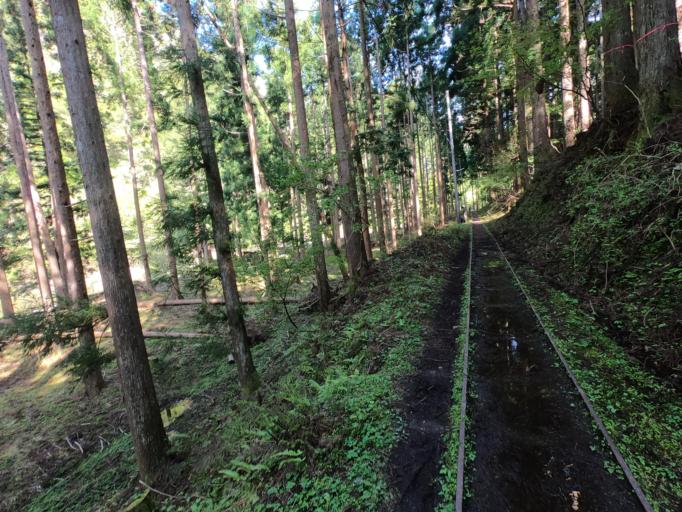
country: JP
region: Fukui
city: Obama
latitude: 35.3075
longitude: 135.7180
